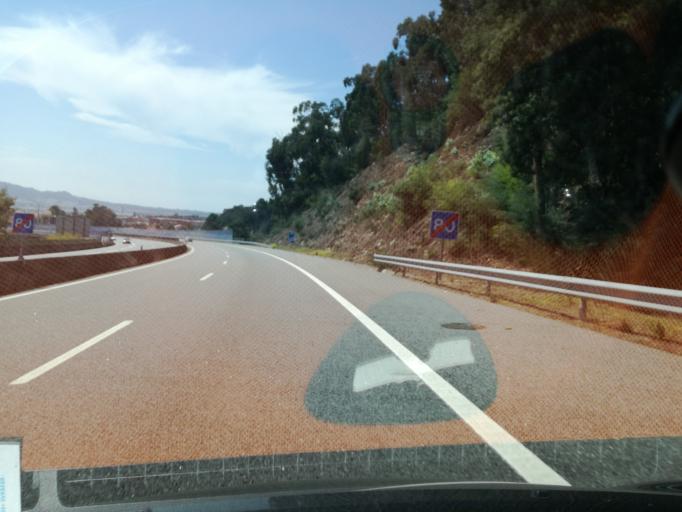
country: PT
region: Viana do Castelo
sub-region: Viana do Castelo
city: Meadela
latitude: 41.7239
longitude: -8.7988
